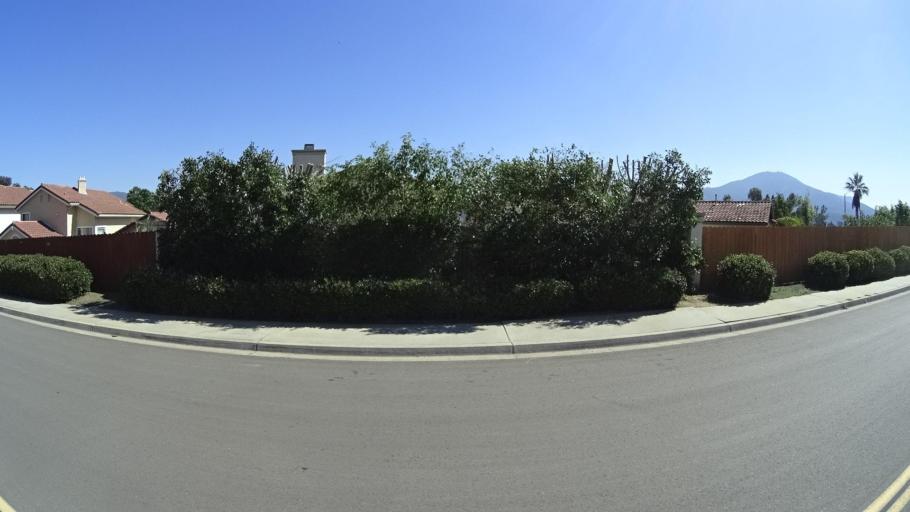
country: US
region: California
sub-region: San Diego County
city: Rancho San Diego
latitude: 32.7502
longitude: -116.9396
